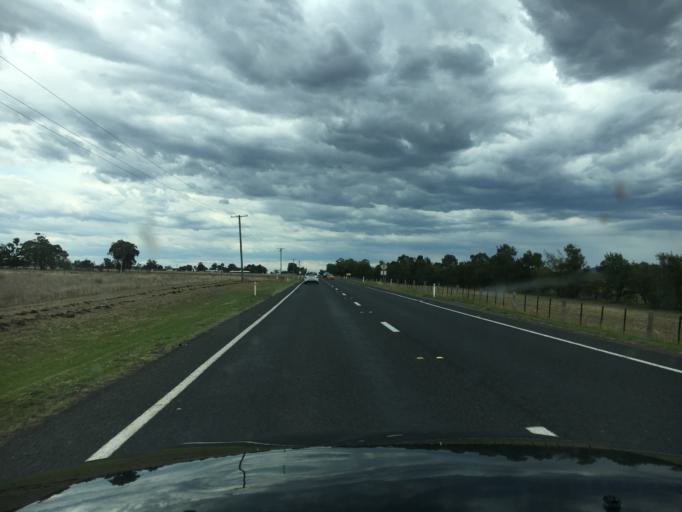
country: AU
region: New South Wales
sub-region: Muswellbrook
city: Muswellbrook
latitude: -32.0101
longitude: 150.8638
